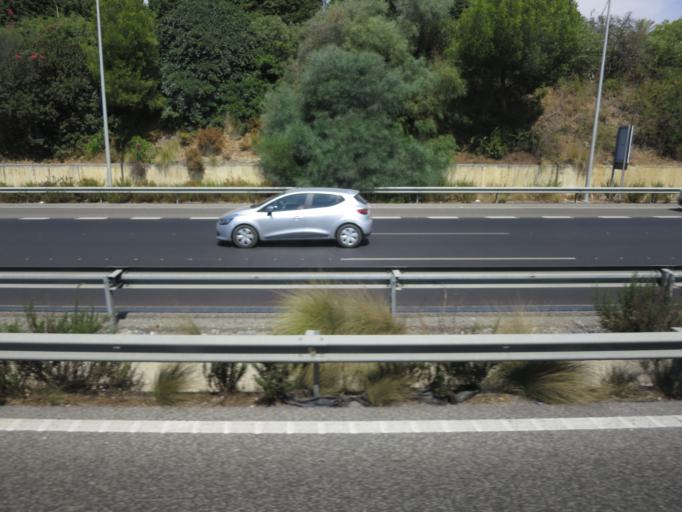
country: ES
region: Andalusia
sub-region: Provincia de Malaga
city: Marbella
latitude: 36.5131
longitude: -4.9226
